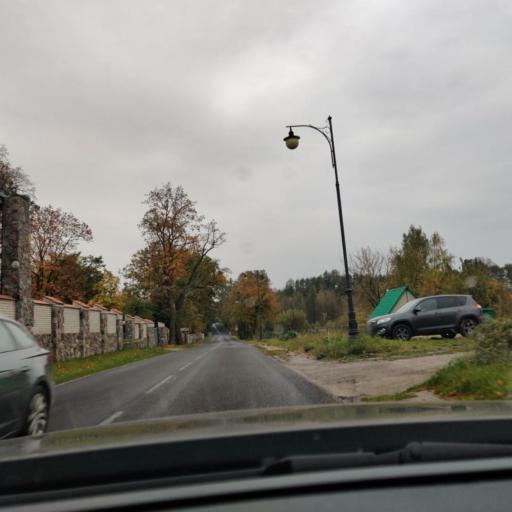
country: PL
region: Masovian Voivodeship
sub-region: Powiat sochaczewski
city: Sochaczew
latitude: 52.2580
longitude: 20.3093
